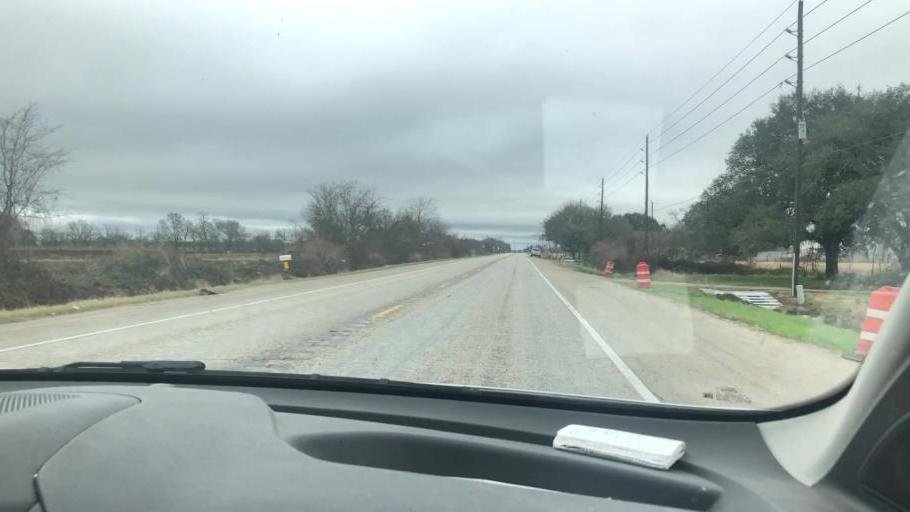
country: US
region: Texas
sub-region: Wharton County
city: Wharton
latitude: 29.2662
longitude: -96.0575
